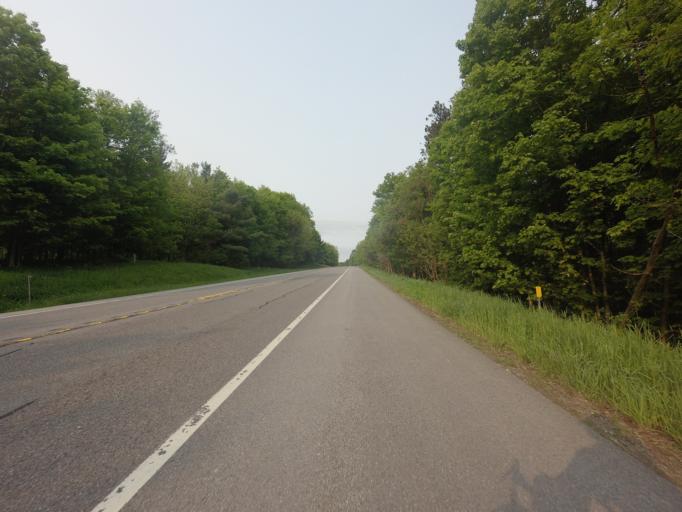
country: US
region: New York
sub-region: Jefferson County
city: Carthage
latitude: 44.0554
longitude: -75.5486
